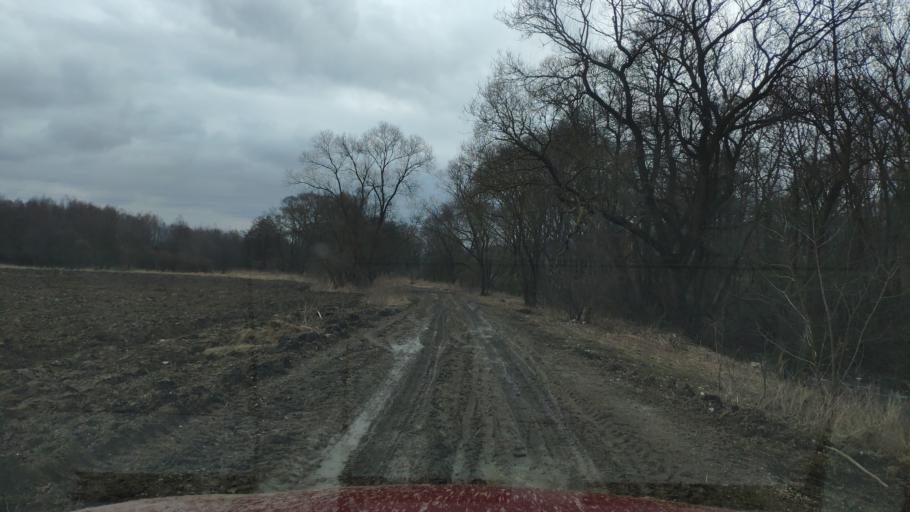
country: SK
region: Presovsky
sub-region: Okres Presov
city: Presov
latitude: 49.0762
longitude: 21.2914
